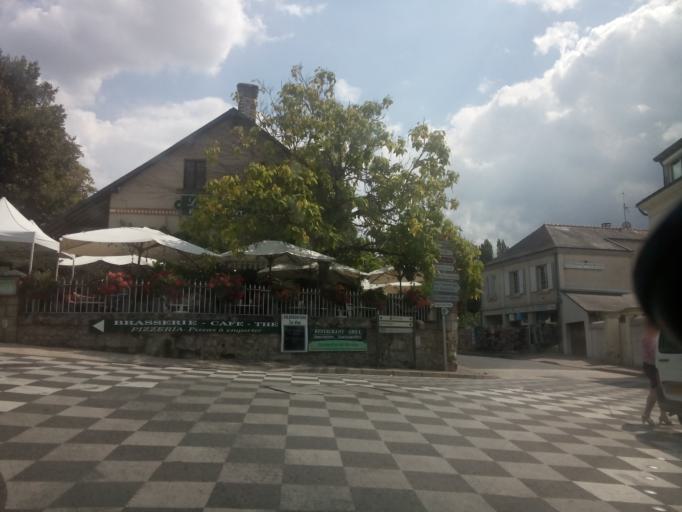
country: FR
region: Centre
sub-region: Departement d'Indre-et-Loire
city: Azay-le-Rideau
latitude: 47.2613
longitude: 0.4672
